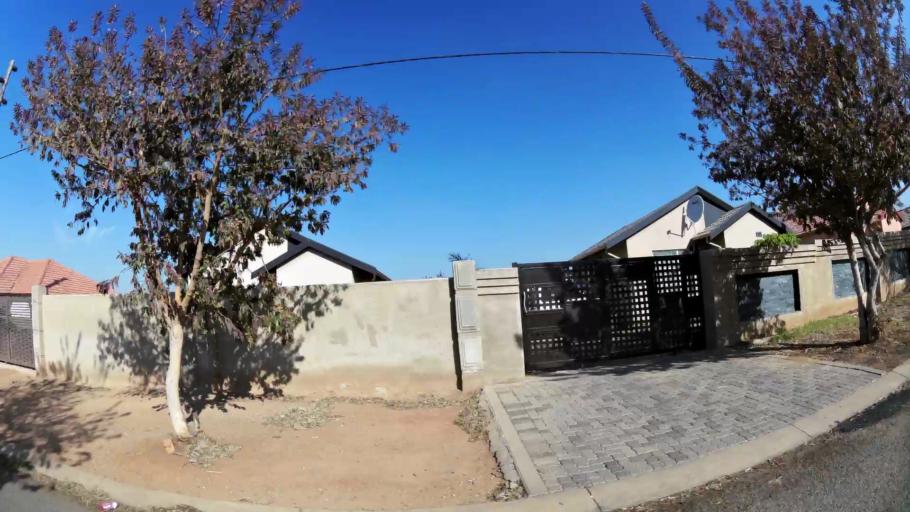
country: ZA
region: Gauteng
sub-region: West Rand District Municipality
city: Muldersdriseloop
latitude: -26.0400
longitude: 27.9118
